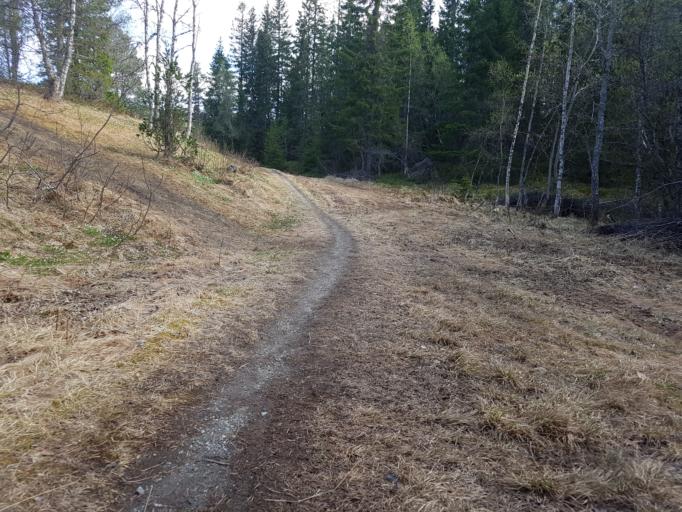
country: NO
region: Sor-Trondelag
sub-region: Trondheim
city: Trondheim
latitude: 63.4424
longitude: 10.2889
